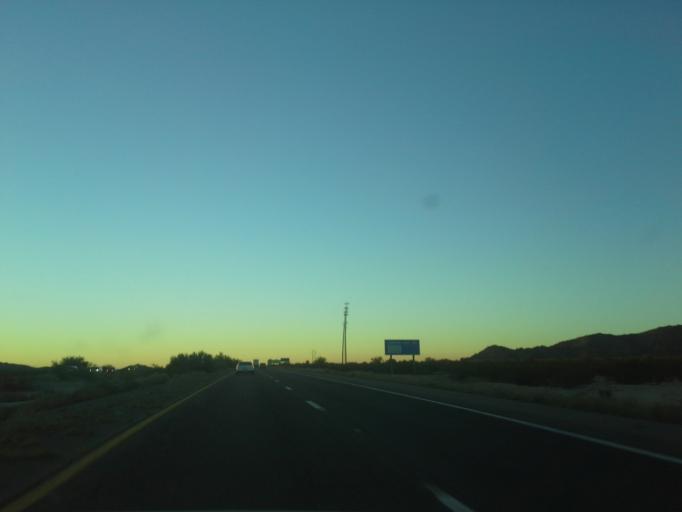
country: US
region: Arizona
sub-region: Pinal County
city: Sacaton
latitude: 32.9897
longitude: -111.7420
